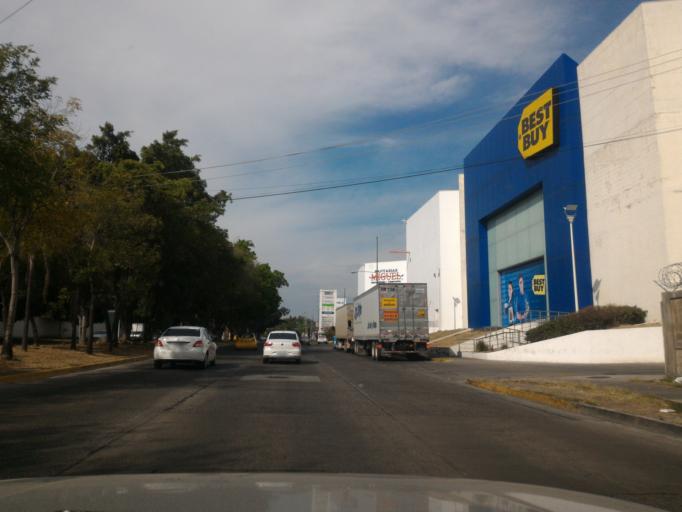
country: MX
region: Jalisco
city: Guadalajara
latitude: 20.6478
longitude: -103.4221
